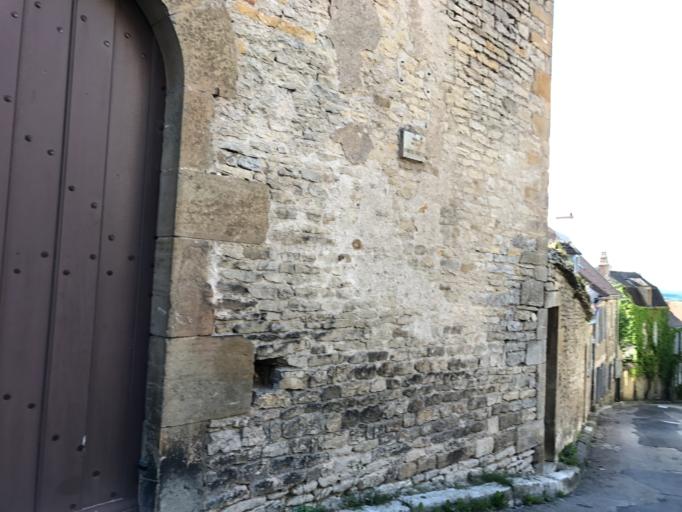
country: FR
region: Bourgogne
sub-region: Departement de l'Yonne
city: Avallon
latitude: 47.4653
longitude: 3.7446
